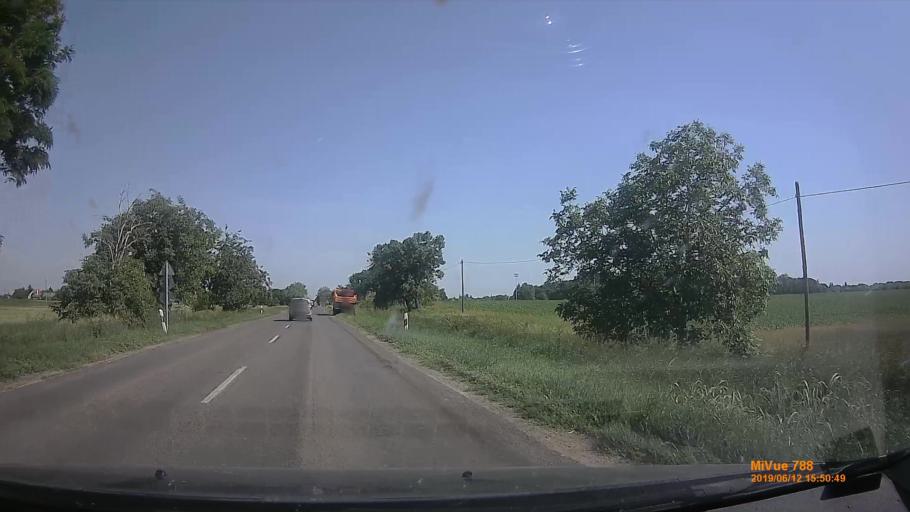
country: HU
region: Csongrad
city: Apatfalva
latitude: 46.1849
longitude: 20.5675
